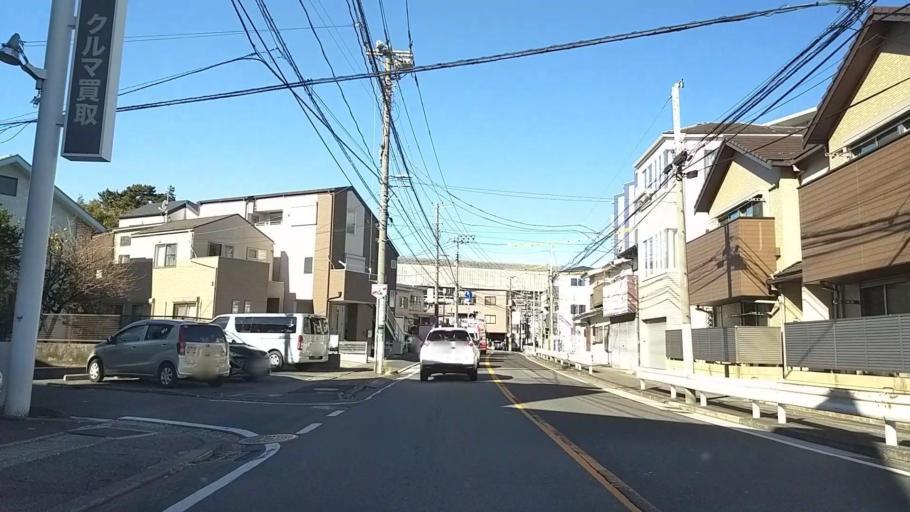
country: JP
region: Kanagawa
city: Yokohama
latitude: 35.4661
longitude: 139.5801
